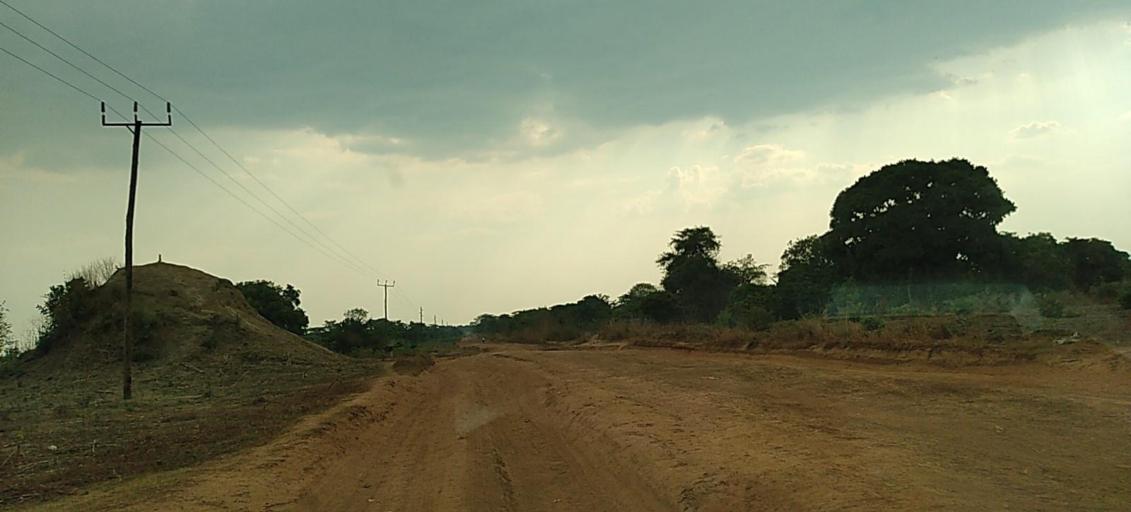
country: ZM
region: Copperbelt
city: Kalulushi
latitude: -12.9479
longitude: 27.9138
